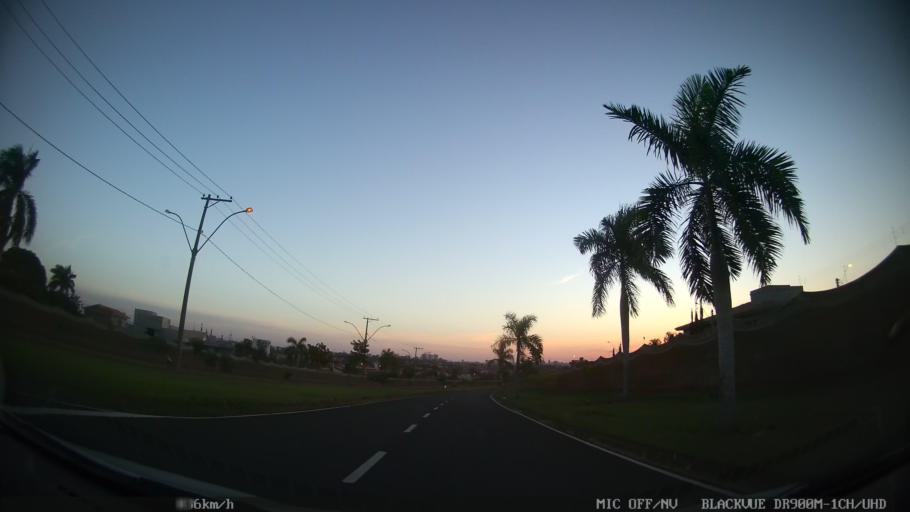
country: BR
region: Sao Paulo
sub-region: Sao Jose Do Rio Preto
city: Sao Jose do Rio Preto
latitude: -20.8168
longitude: -49.3407
